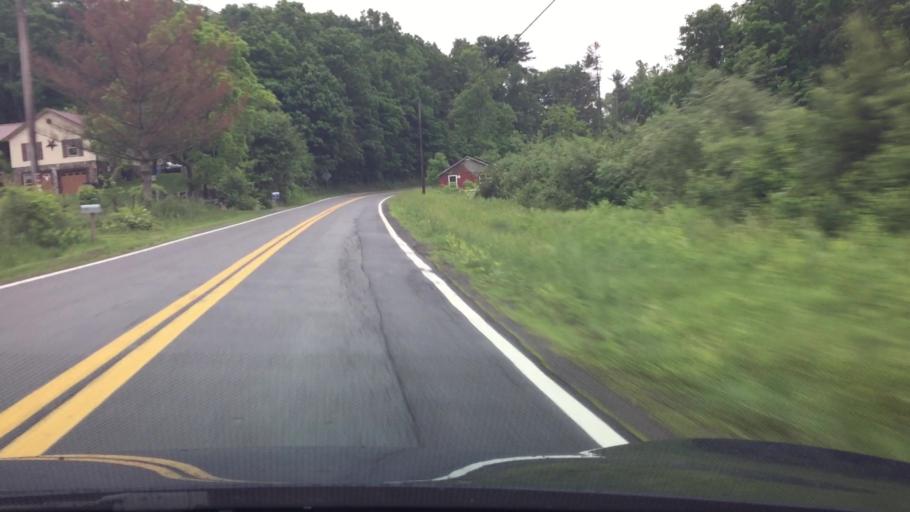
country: US
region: West Virginia
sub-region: Summers County
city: Hinton
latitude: 37.5769
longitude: -80.7873
